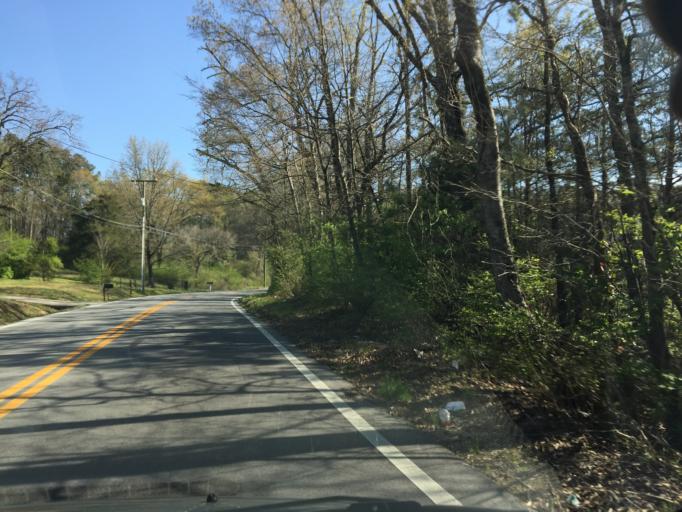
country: US
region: Tennessee
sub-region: Hamilton County
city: East Chattanooga
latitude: 35.0717
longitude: -85.2071
